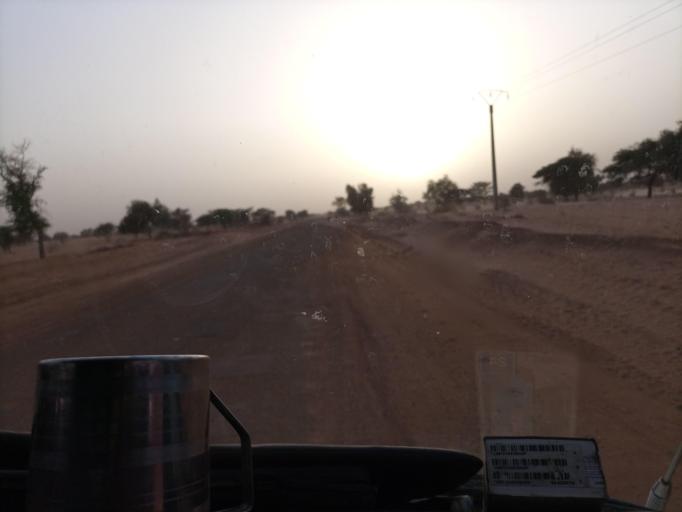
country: SN
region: Louga
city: Dara
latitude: 15.4071
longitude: -15.6727
